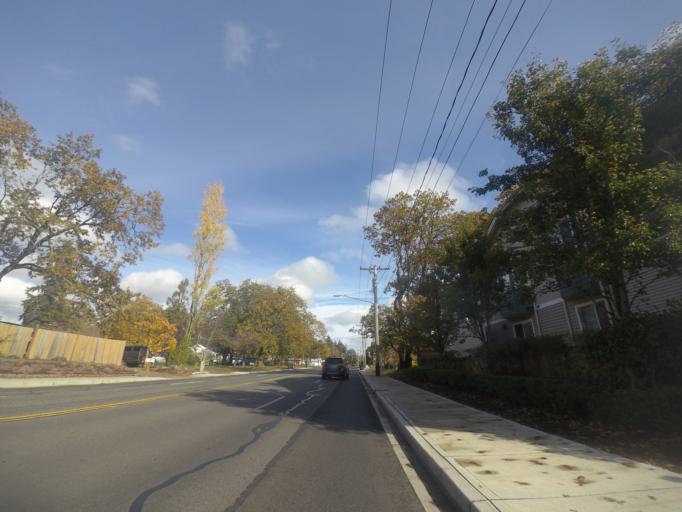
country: US
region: Washington
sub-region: Pierce County
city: Lakewood
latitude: 47.1749
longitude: -122.5132
